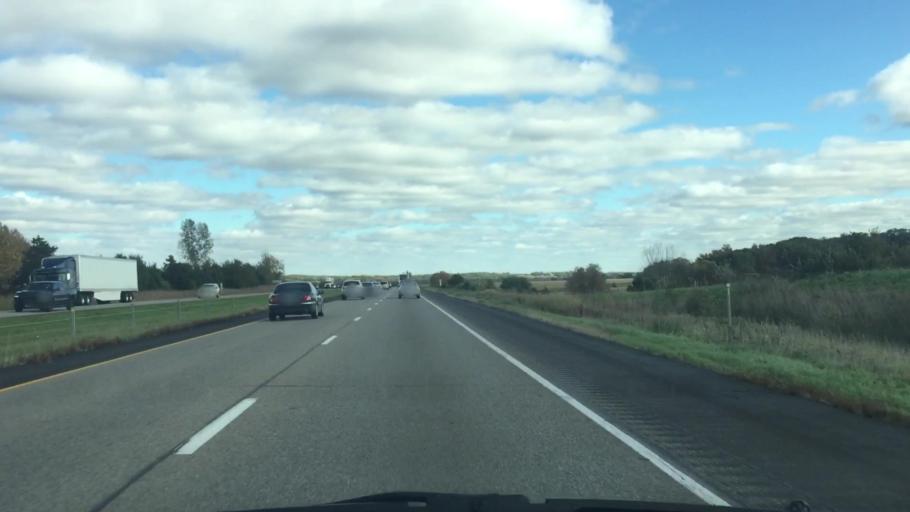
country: US
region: Iowa
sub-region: Muscatine County
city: West Liberty
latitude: 41.6483
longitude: -91.1712
